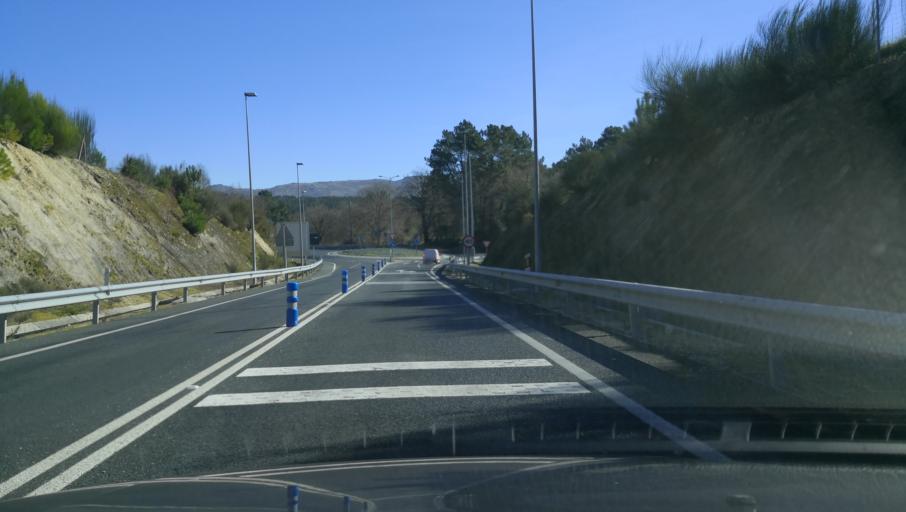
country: ES
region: Galicia
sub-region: Provincia de Ourense
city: Pinor
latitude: 42.5240
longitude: -8.0109
